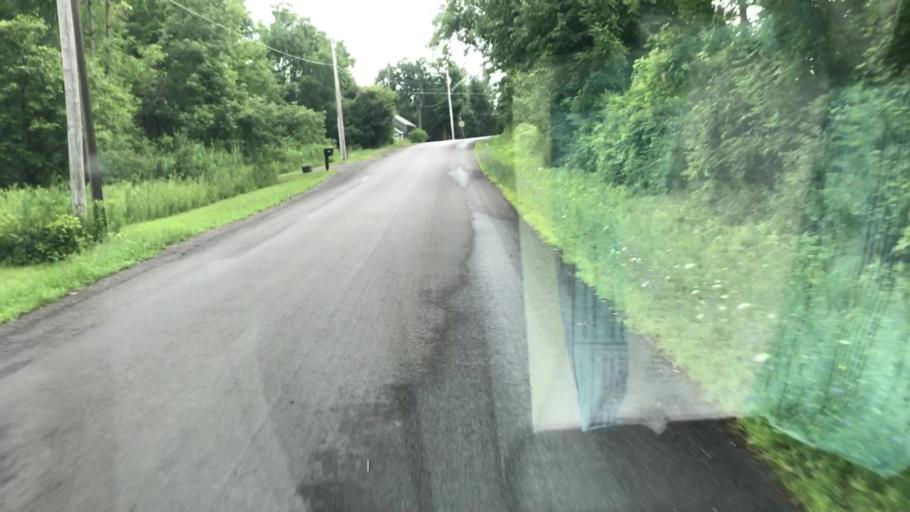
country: US
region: New York
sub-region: Onondaga County
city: Manlius
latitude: 42.9802
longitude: -75.9831
